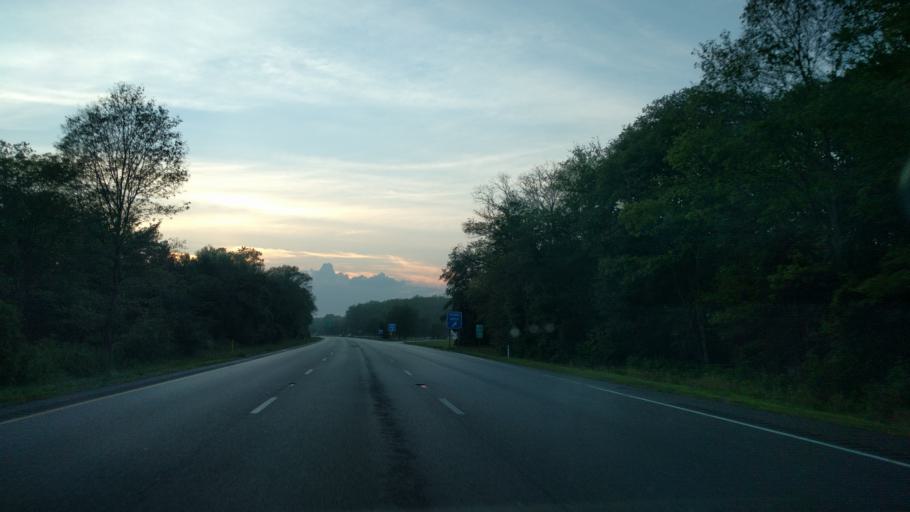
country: US
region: Massachusetts
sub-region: Bristol County
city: Ocean Grove
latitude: 41.7656
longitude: -71.2368
